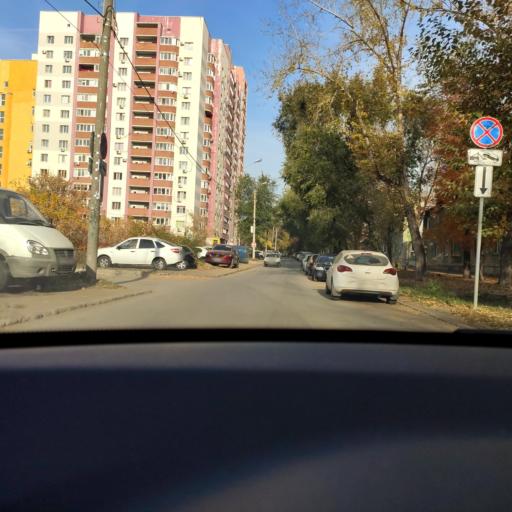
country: RU
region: Samara
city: Samara
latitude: 53.2215
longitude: 50.2462
